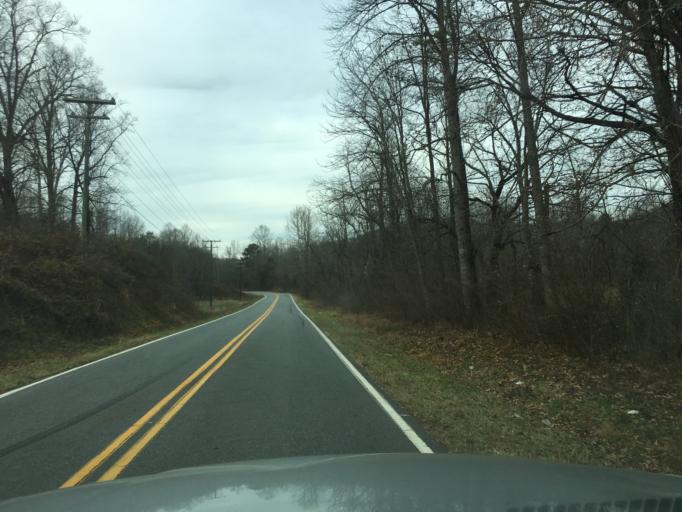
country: US
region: North Carolina
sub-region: McDowell County
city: West Marion
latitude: 35.6280
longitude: -81.9823
